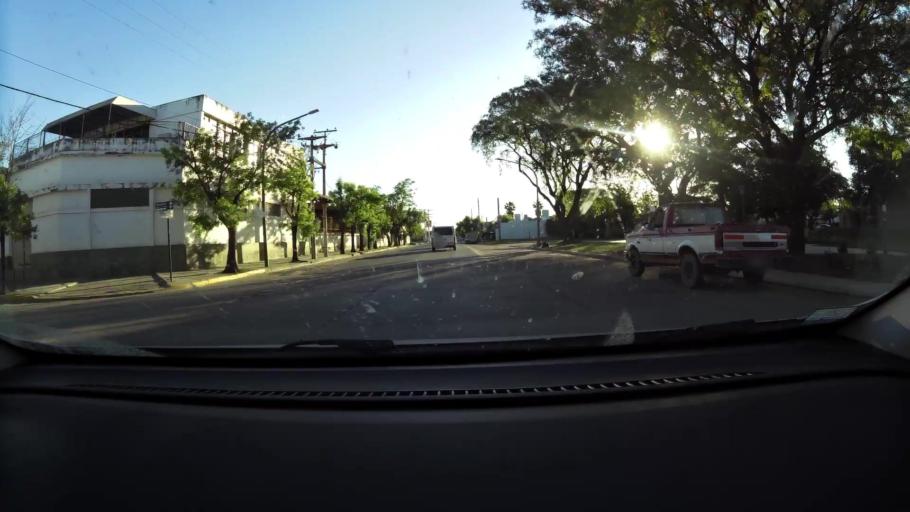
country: AR
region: Cordoba
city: Las Varillas
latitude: -31.8745
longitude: -62.7157
